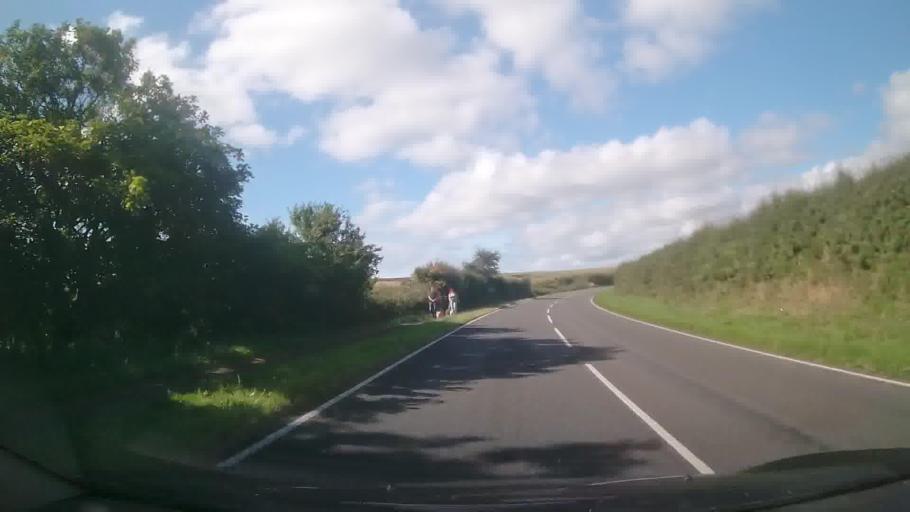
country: GB
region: Wales
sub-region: Pembrokeshire
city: Penally
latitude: 51.6573
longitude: -4.7248
